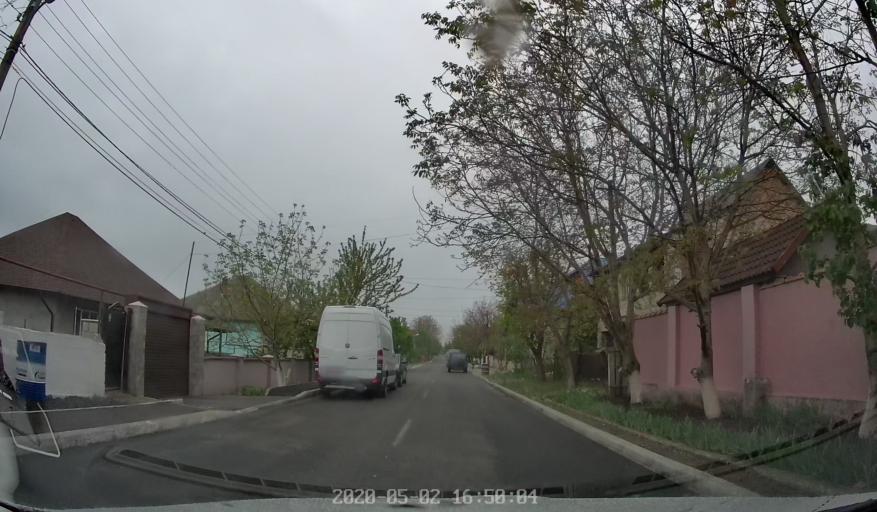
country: MD
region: Chisinau
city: Chisinau
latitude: 46.9674
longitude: 28.8283
